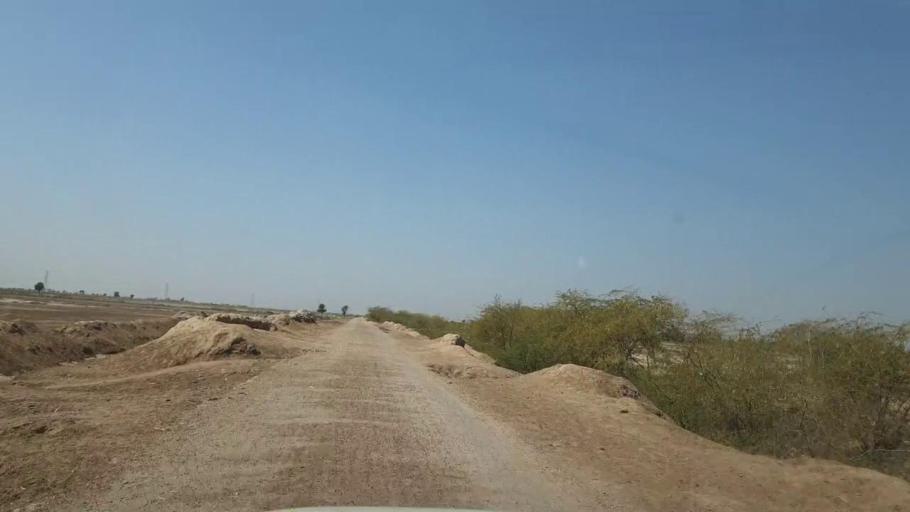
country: PK
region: Sindh
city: Kunri
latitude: 25.0963
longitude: 69.5102
